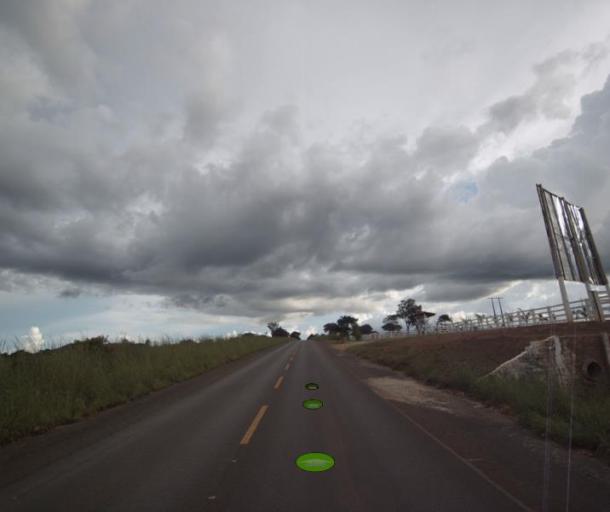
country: BR
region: Goias
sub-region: Niquelandia
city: Niquelandia
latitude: -14.4894
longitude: -48.4896
